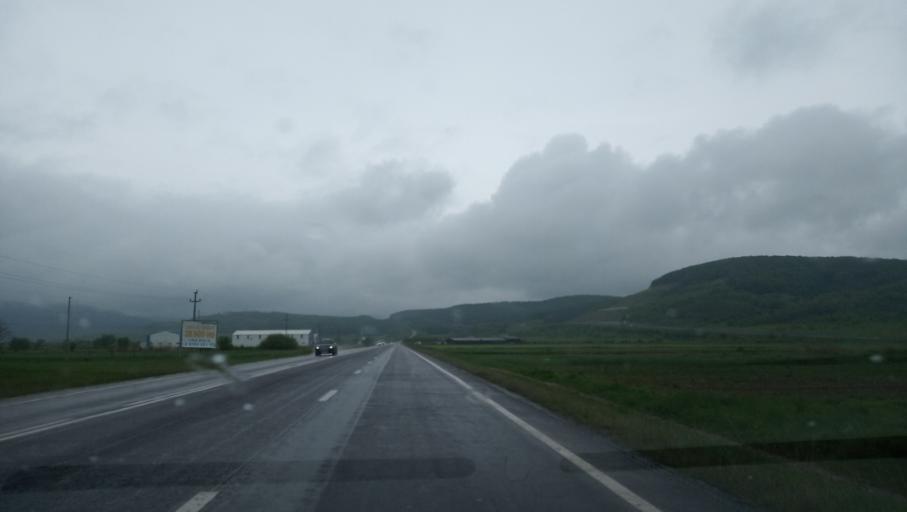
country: RO
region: Sibiu
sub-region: Comuna Cristian
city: Cristian
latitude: 45.7843
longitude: 23.9978
